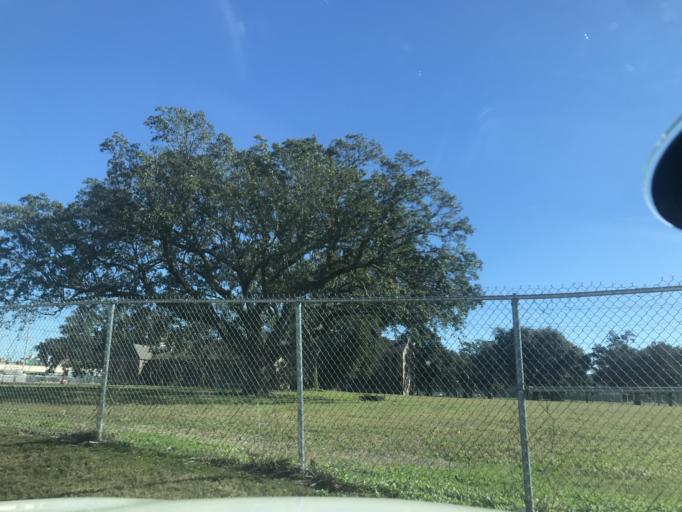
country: US
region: Louisiana
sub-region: Orleans Parish
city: New Orleans
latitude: 29.9520
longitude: -90.0928
